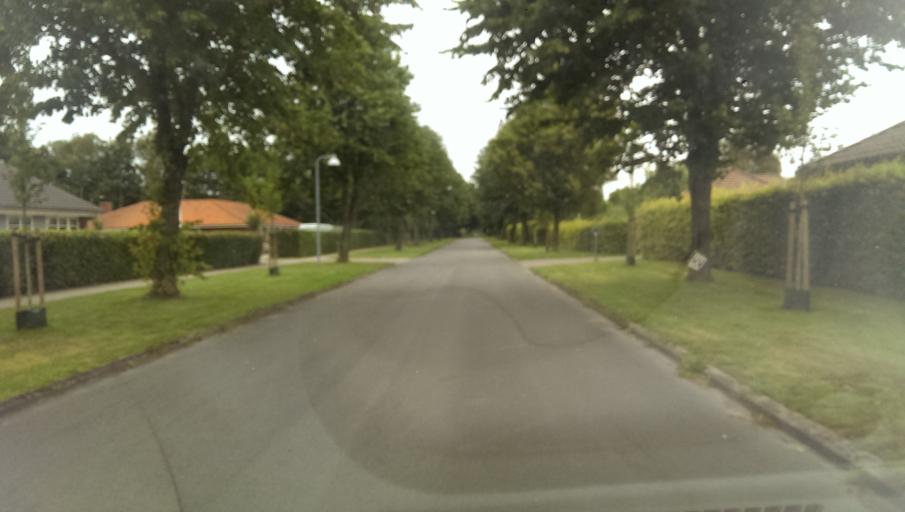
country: DK
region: South Denmark
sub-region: Esbjerg Kommune
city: Bramming
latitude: 55.4752
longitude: 8.6891
